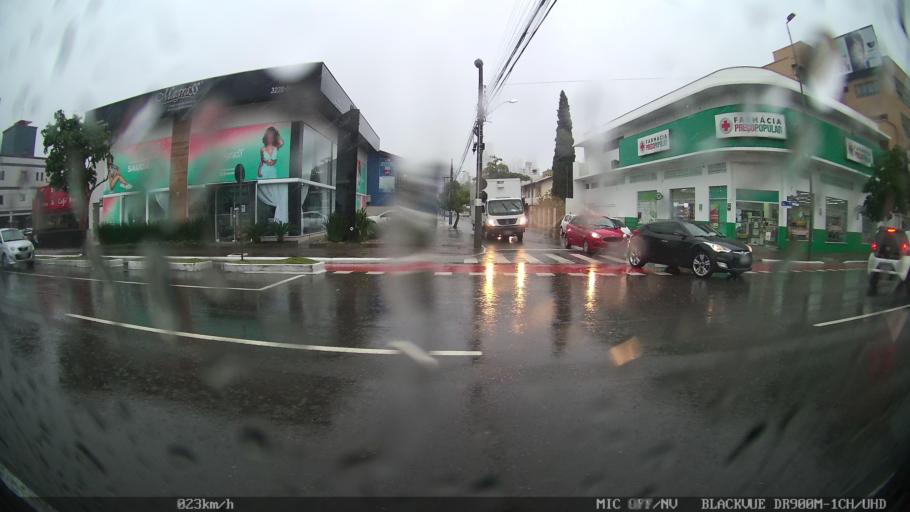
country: BR
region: Santa Catarina
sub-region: Balneario Camboriu
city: Balneario Camboriu
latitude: -26.9986
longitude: -48.6380
